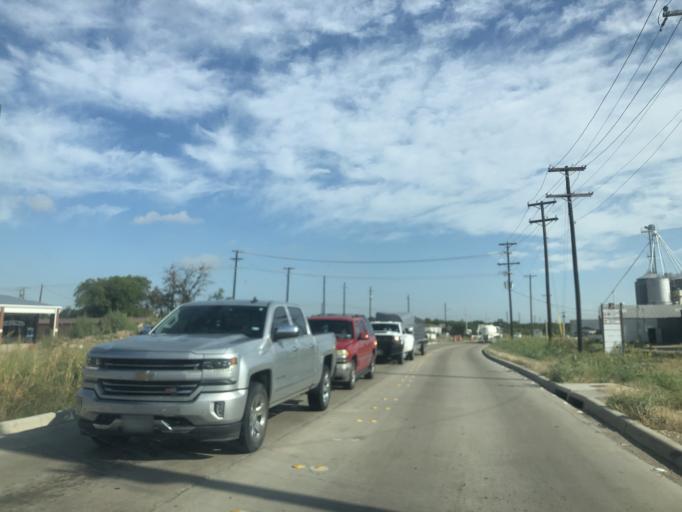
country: US
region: Texas
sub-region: Denton County
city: Justin
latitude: 33.0884
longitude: -97.2953
